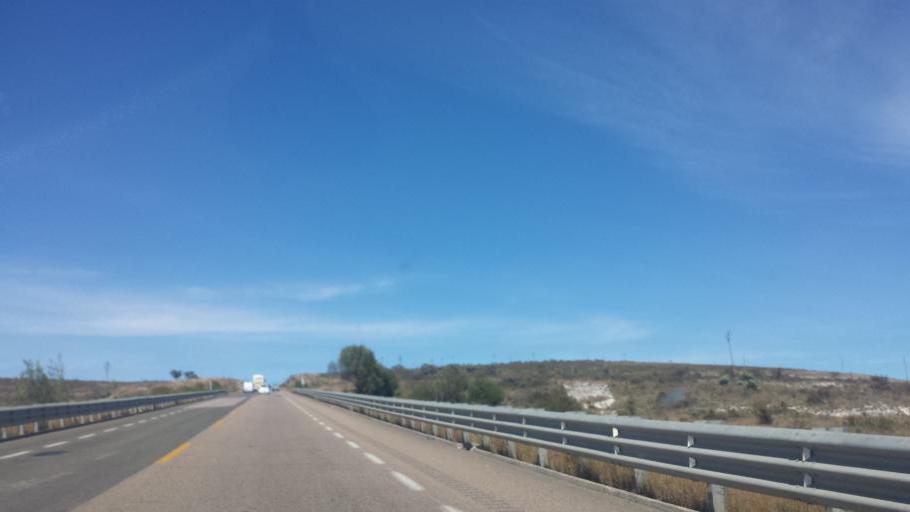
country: MX
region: Oaxaca
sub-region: Villa Tejupam de la Union
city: Villa Tejupam de la Union
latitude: 17.7674
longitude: -97.3573
